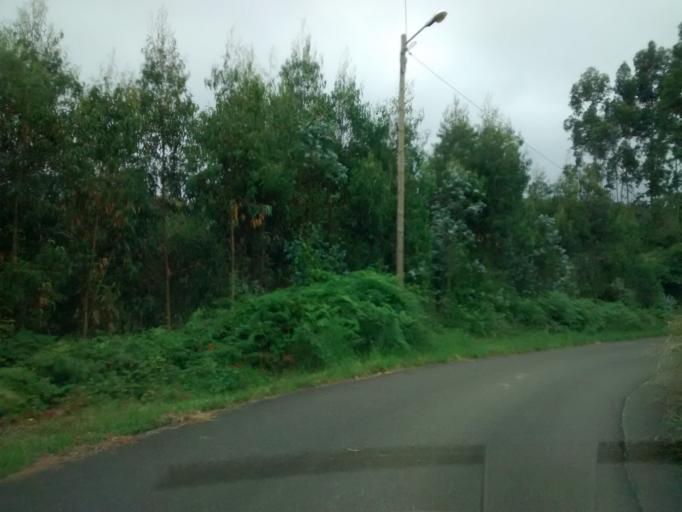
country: ES
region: Asturias
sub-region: Province of Asturias
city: Villaviciosa
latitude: 43.5423
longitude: -5.4080
